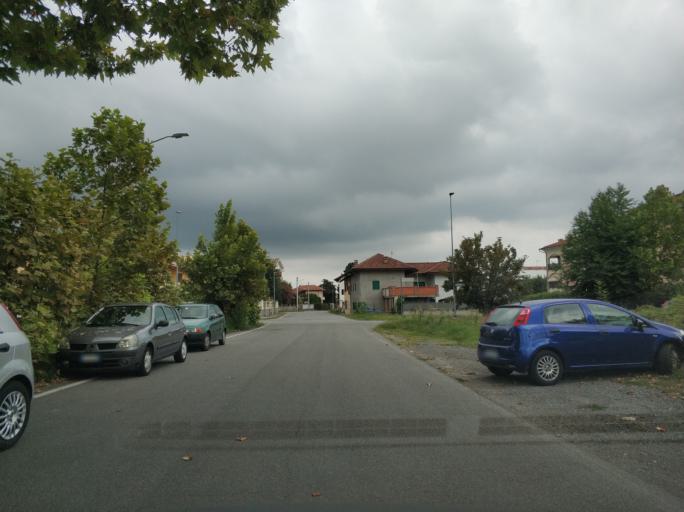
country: IT
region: Piedmont
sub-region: Provincia di Torino
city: Caselle Torinese
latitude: 45.1760
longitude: 7.6321
